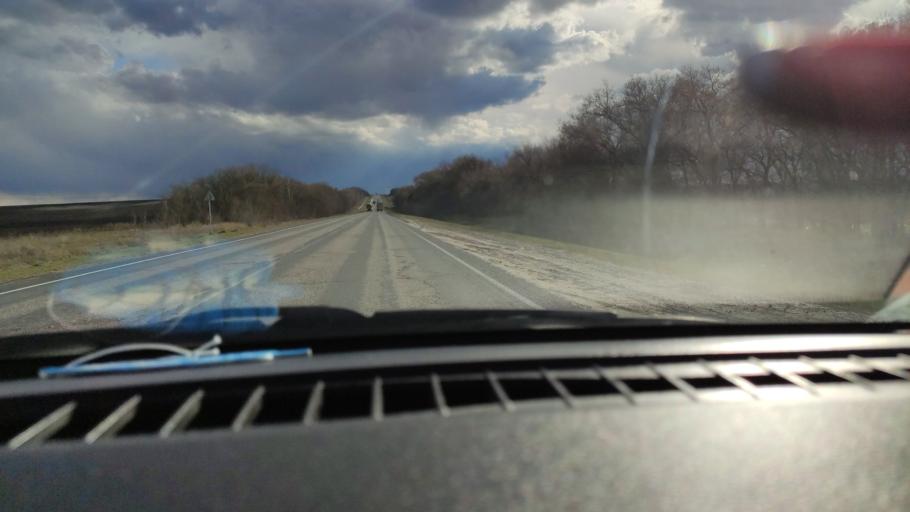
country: RU
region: Saratov
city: Sinodskoye
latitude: 51.9653
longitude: 46.6322
